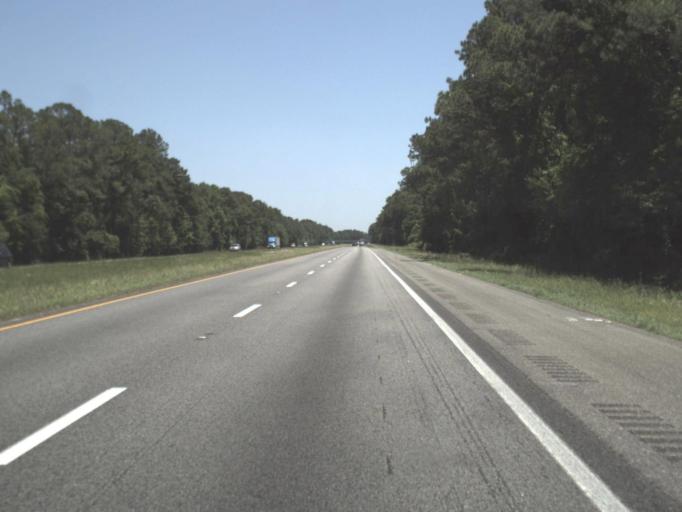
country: US
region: Florida
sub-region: Jefferson County
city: Monticello
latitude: 30.4727
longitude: -83.8410
